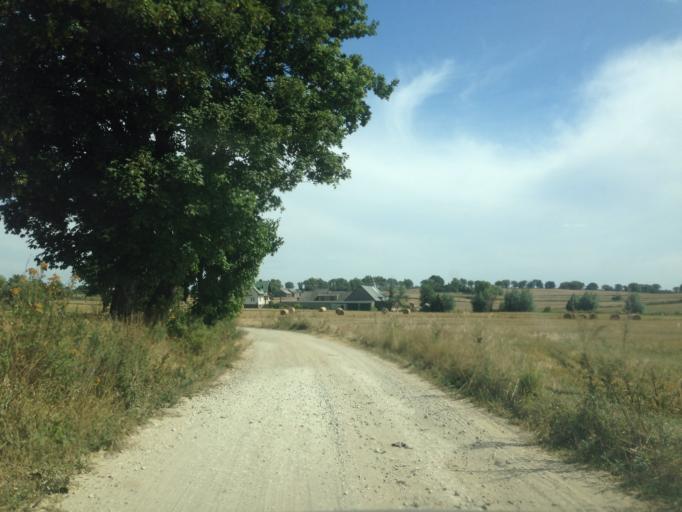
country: PL
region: Kujawsko-Pomorskie
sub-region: Powiat brodnicki
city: Bartniczka
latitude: 53.2260
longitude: 19.6220
